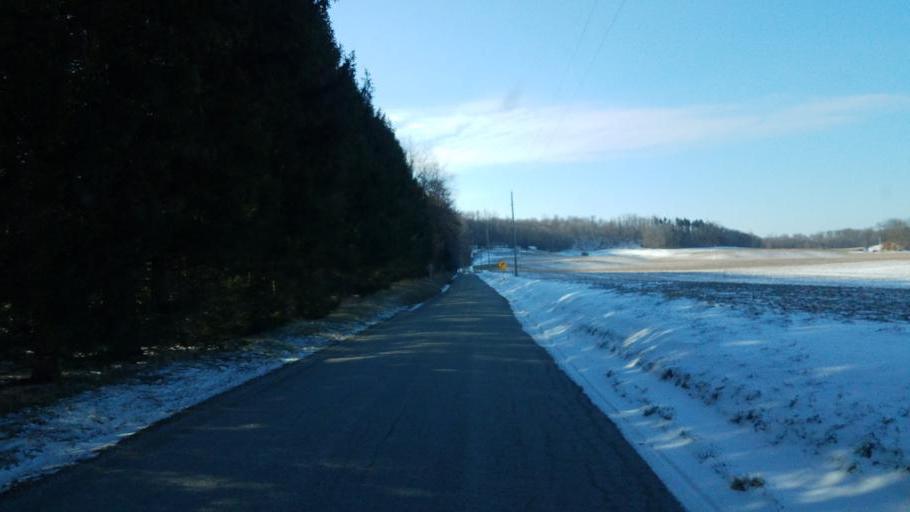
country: US
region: Ohio
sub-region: Sandusky County
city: Bellville
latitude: 40.6196
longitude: -82.5530
